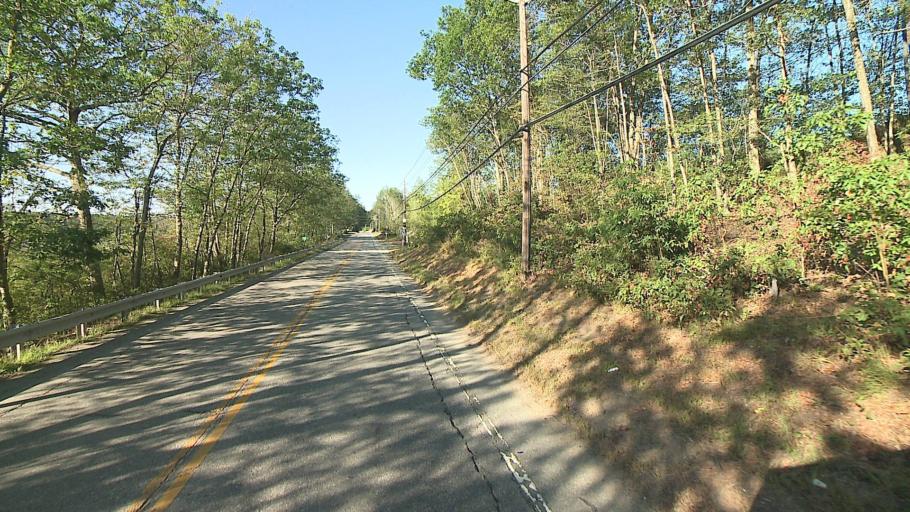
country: US
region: Connecticut
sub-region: New London County
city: Jewett City
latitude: 41.6263
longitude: -71.9691
